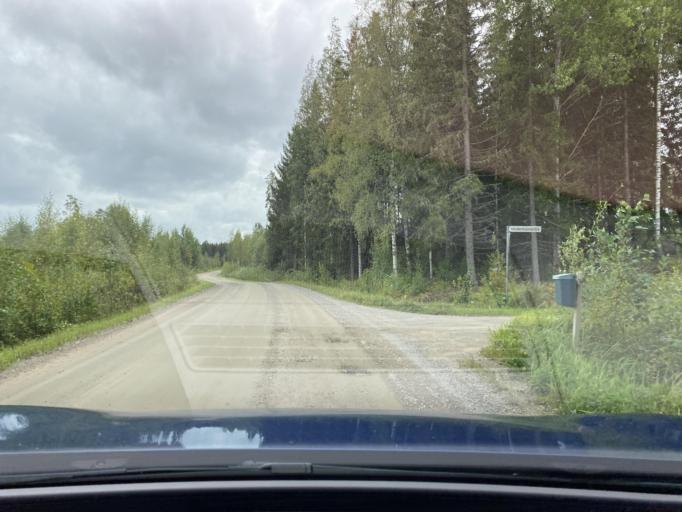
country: FI
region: Pirkanmaa
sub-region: Lounais-Pirkanmaa
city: Punkalaidun
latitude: 61.2212
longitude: 23.1619
